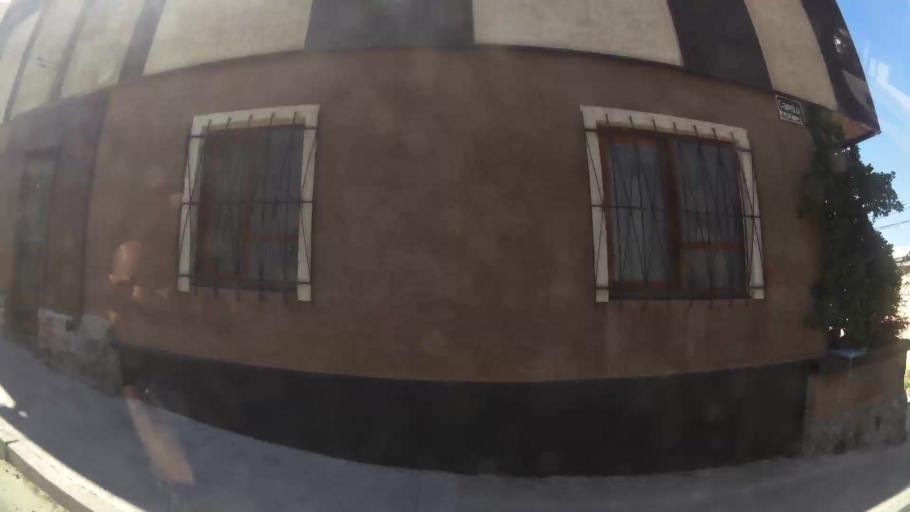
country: CL
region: Valparaiso
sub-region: Provincia de Valparaiso
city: Valparaiso
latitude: -33.0237
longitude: -71.6349
